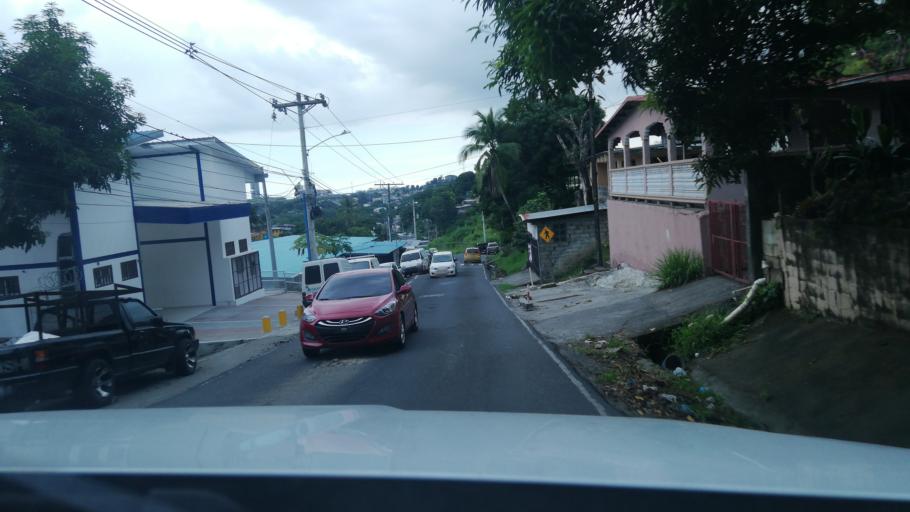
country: PA
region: Panama
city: San Miguelito
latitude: 9.0500
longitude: -79.4929
